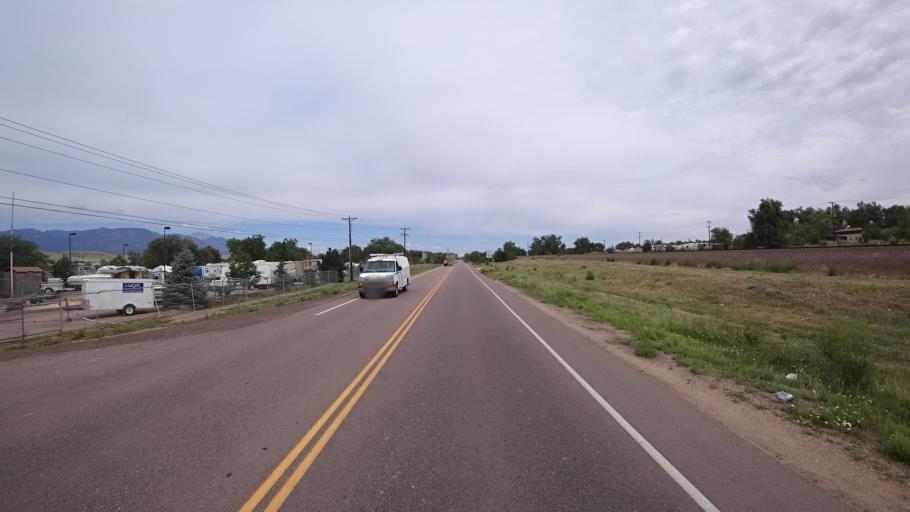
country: US
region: Colorado
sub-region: El Paso County
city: Fountain
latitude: 38.6992
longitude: -104.7068
